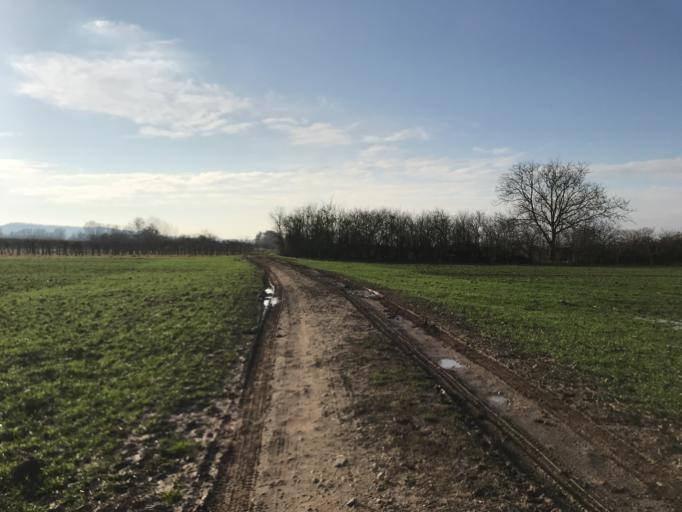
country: DE
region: Hesse
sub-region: Regierungsbezirk Darmstadt
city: Eltville
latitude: 50.0137
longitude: 8.1310
